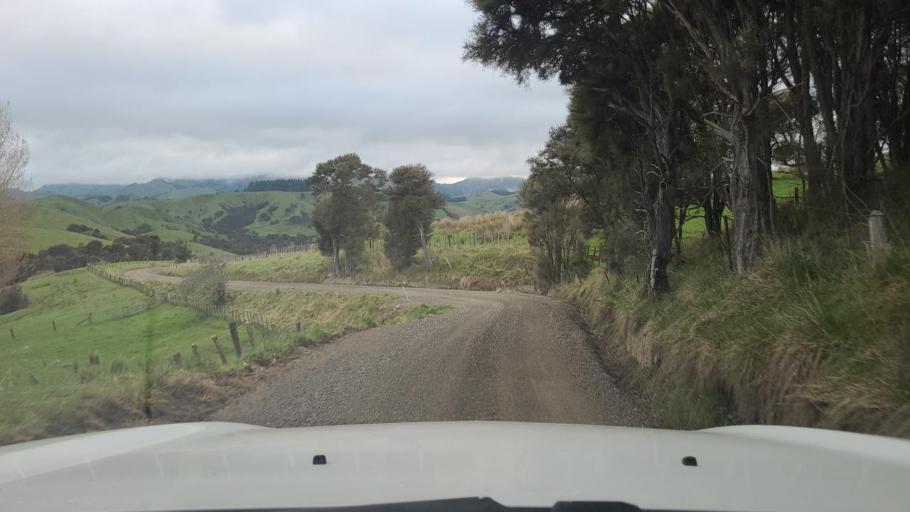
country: NZ
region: Wellington
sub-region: Masterton District
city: Masterton
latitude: -41.1640
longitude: 175.6893
